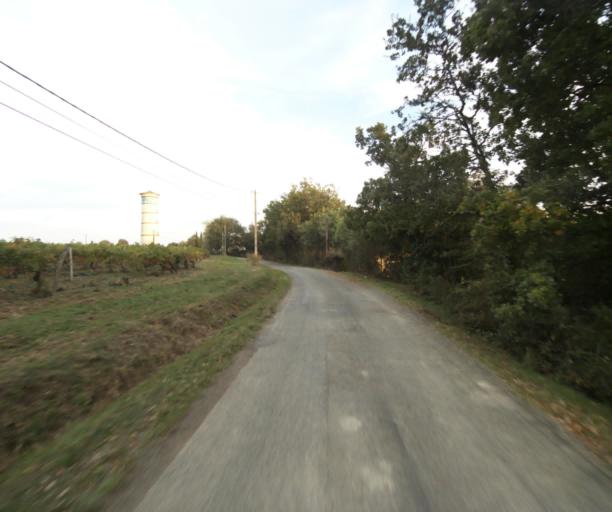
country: FR
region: Midi-Pyrenees
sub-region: Departement du Tarn-et-Garonne
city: Pompignan
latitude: 43.8227
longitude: 1.3156
